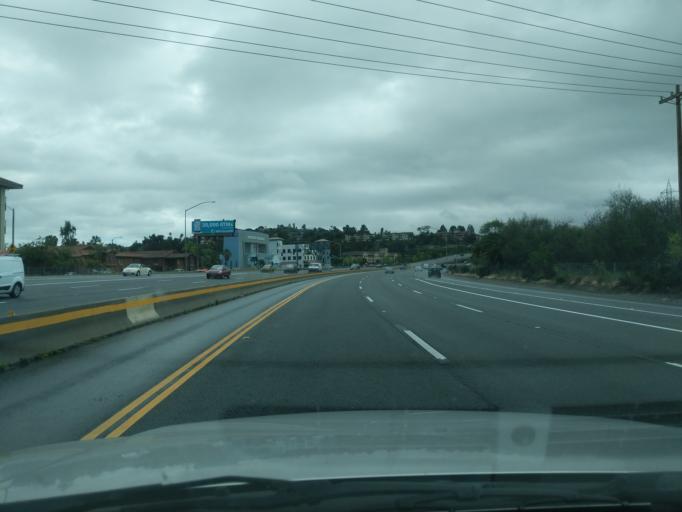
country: US
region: California
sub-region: San Diego County
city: Carlsbad
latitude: 33.1821
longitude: -117.3250
